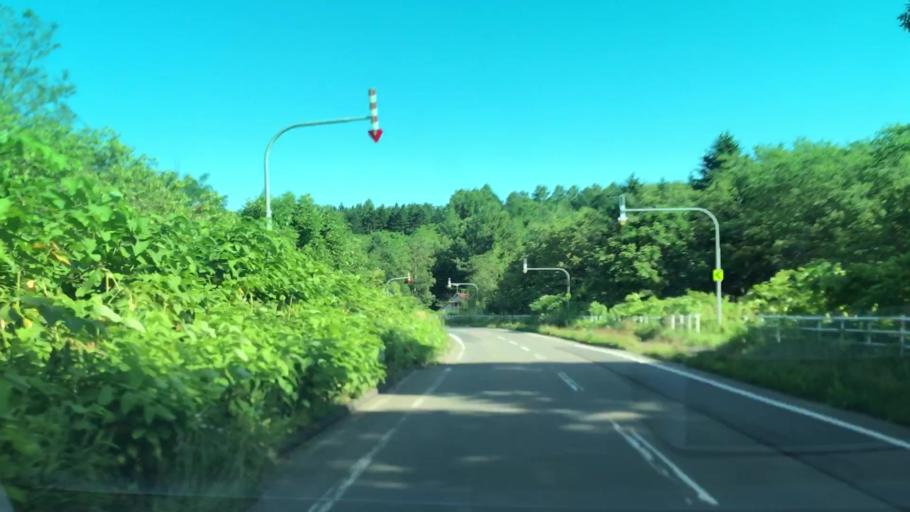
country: JP
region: Hokkaido
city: Yoichi
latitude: 43.0655
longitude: 140.7069
